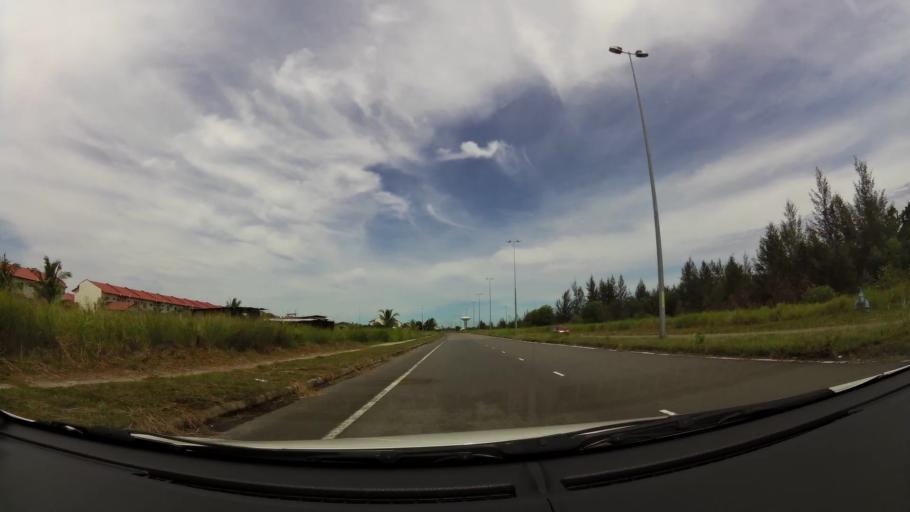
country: BN
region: Belait
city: Kuala Belait
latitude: 4.5915
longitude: 114.2711
